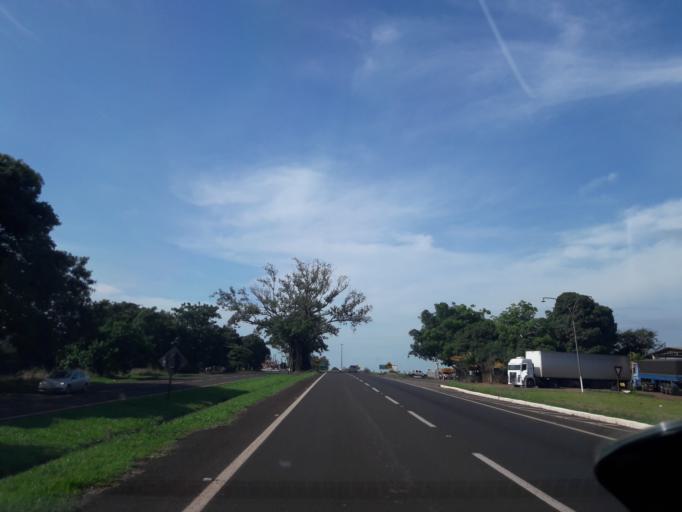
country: BR
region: Parana
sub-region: Paicandu
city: Paicandu
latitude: -23.6109
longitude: -52.0876
